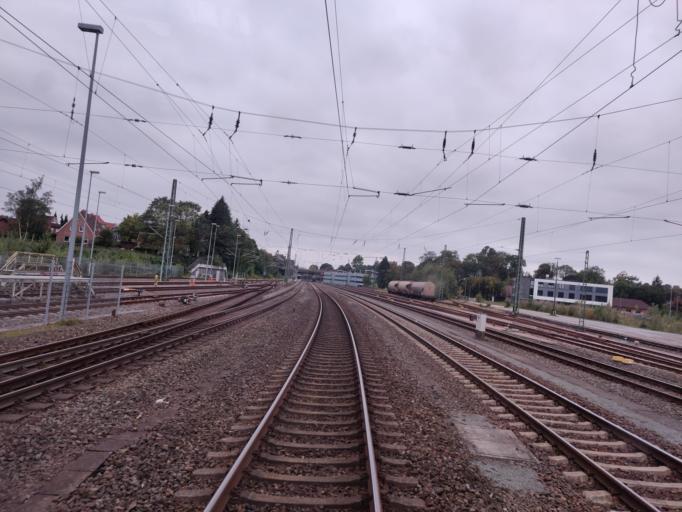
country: DE
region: Lower Saxony
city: Stade
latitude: 53.5950
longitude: 9.4843
